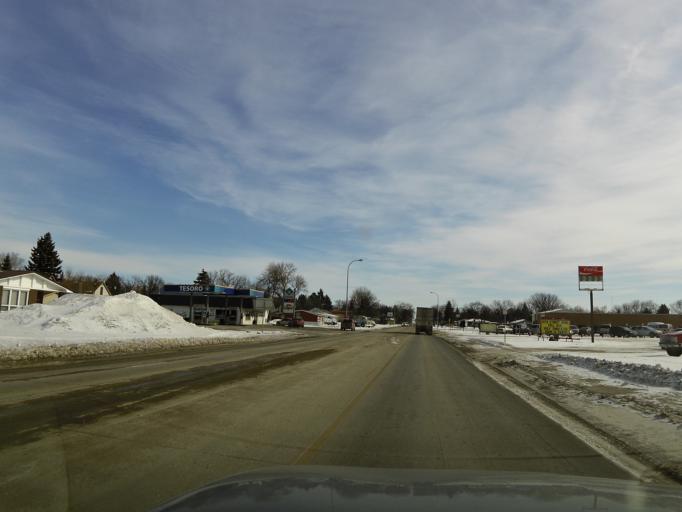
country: US
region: North Dakota
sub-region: Walsh County
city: Grafton
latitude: 48.4125
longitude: -97.4216
